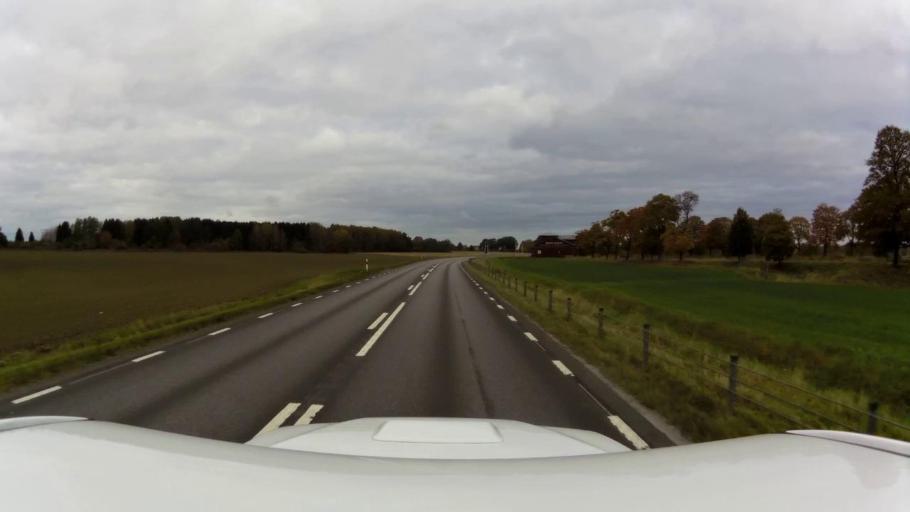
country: SE
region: OEstergoetland
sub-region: Linkopings Kommun
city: Ljungsbro
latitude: 58.5171
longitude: 15.4308
